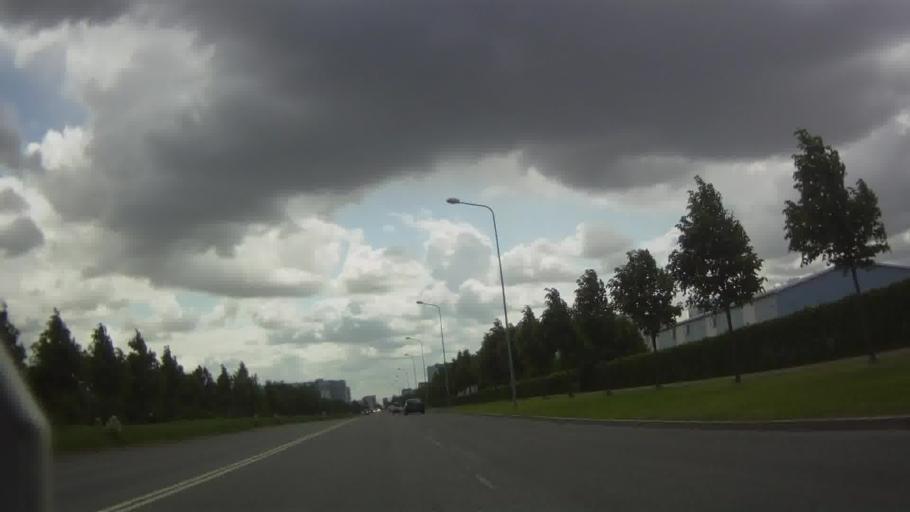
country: LV
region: Stopini
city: Ulbroka
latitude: 56.9500
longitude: 24.2197
